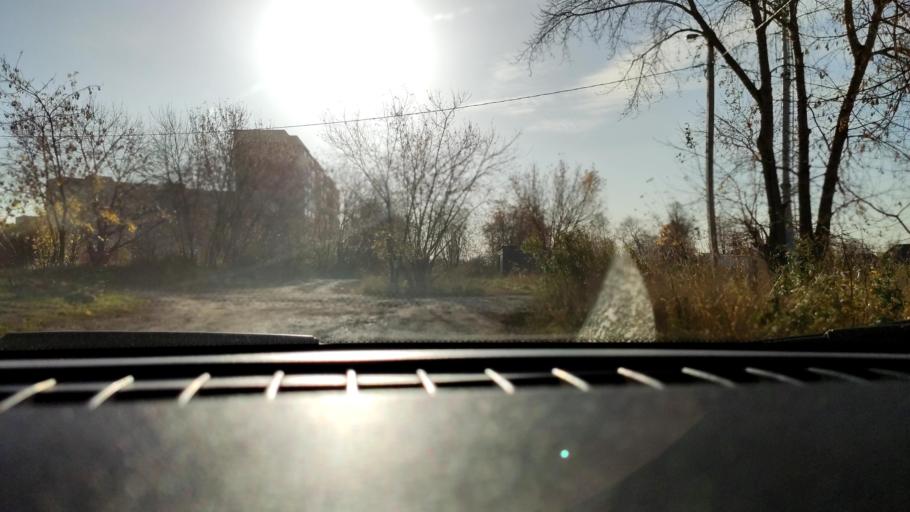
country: RU
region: Perm
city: Perm
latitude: 58.0311
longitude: 56.3193
